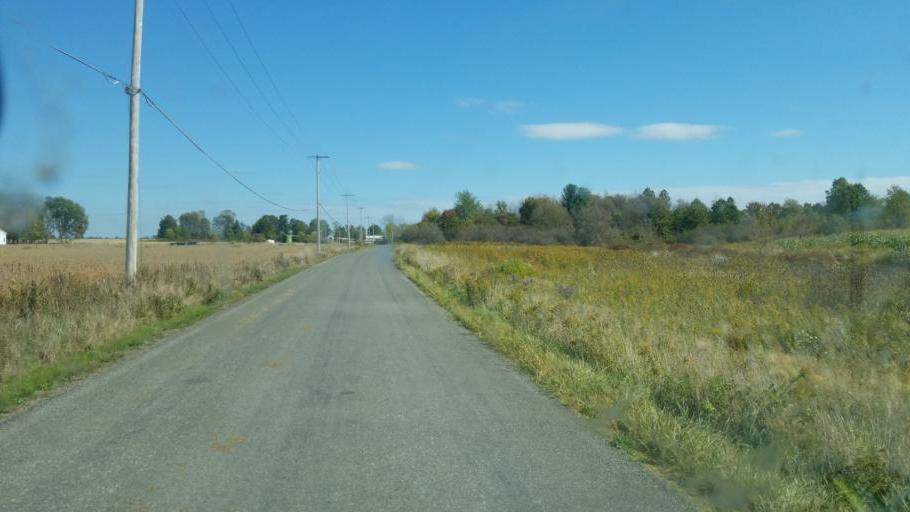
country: US
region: Pennsylvania
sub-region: Mercer County
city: Reynolds Heights
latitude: 41.3295
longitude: -80.3073
